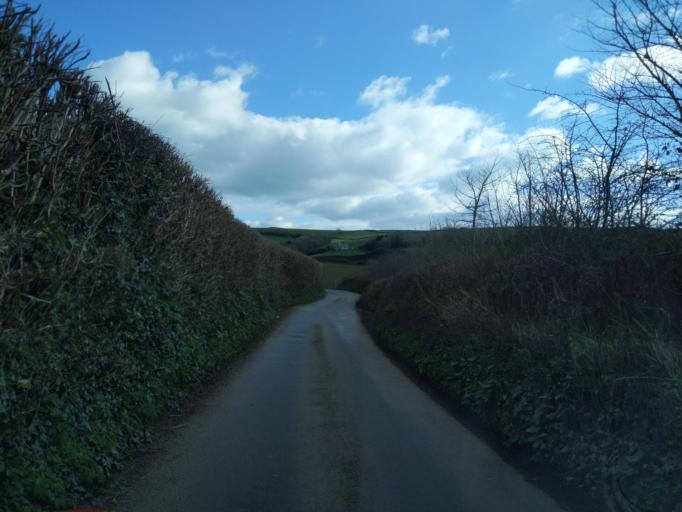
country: GB
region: England
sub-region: Devon
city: Salcombe
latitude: 50.2535
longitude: -3.7040
